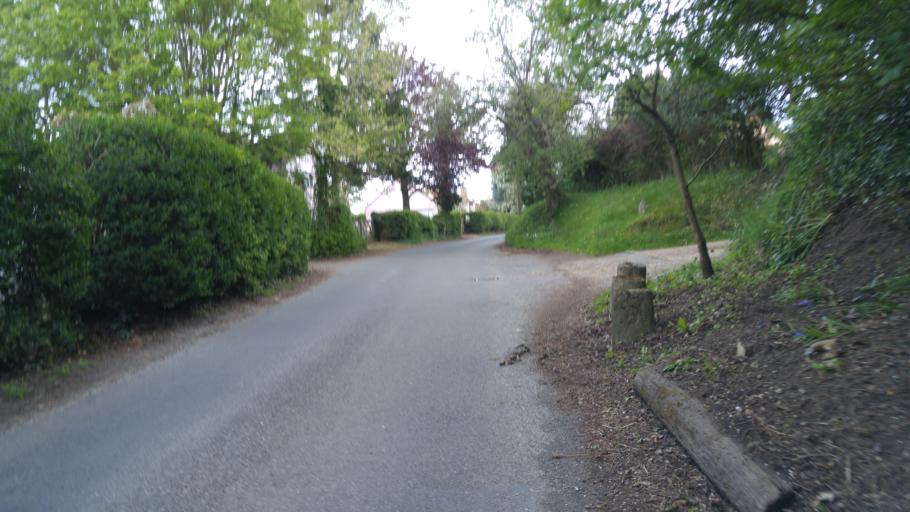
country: GB
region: England
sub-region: Suffolk
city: Sudbury
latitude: 51.9868
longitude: 0.7493
